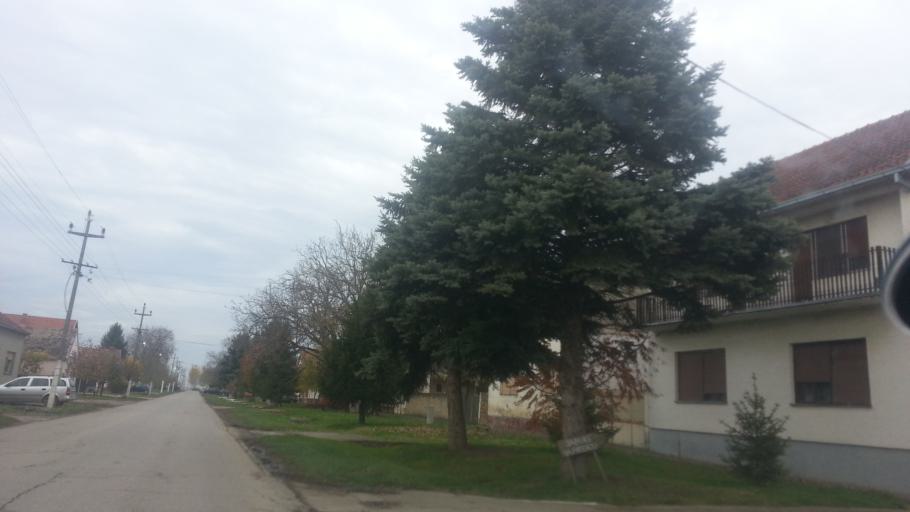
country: RS
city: Golubinci
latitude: 44.9942
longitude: 20.0614
